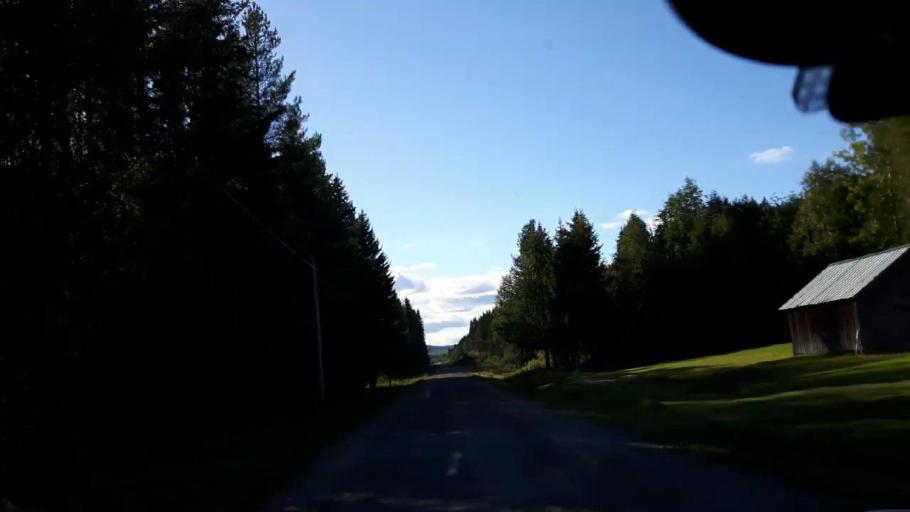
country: SE
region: Jaemtland
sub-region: Ragunda Kommun
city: Hammarstrand
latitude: 63.4876
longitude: 16.0925
